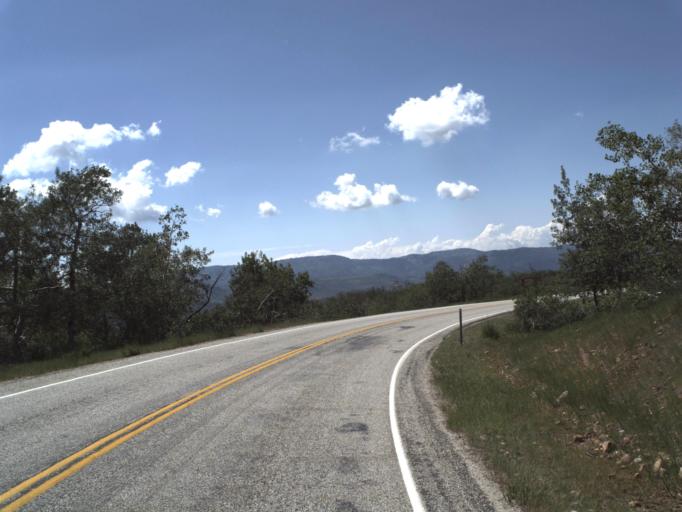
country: US
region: Utah
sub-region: Weber County
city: Wolf Creek
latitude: 41.4063
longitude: -111.5494
